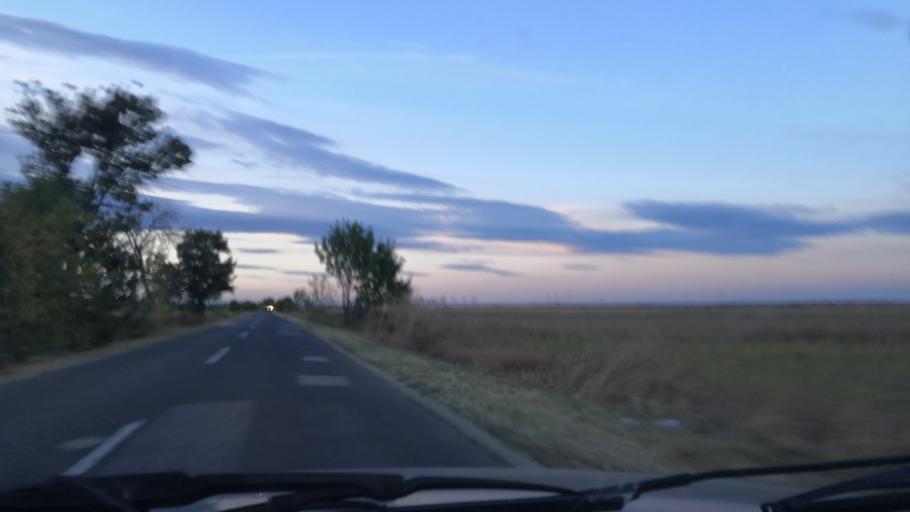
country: RS
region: Central Serbia
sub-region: Borski Okrug
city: Negotin
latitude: 44.2761
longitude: 22.5562
